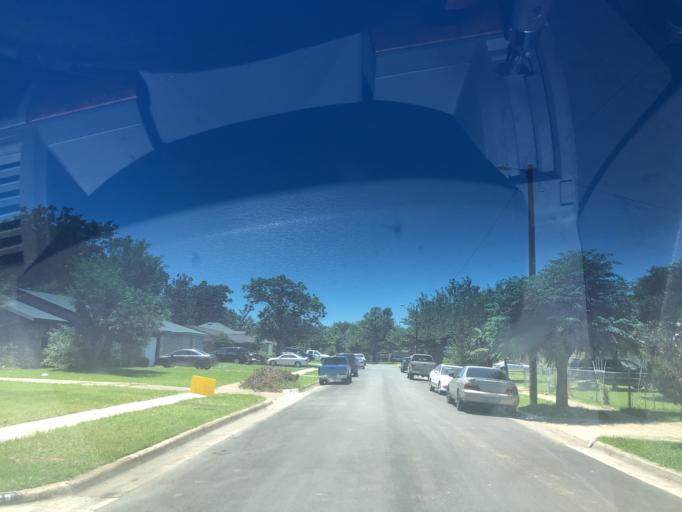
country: US
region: Texas
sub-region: Dallas County
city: Grand Prairie
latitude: 32.7168
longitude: -97.0045
